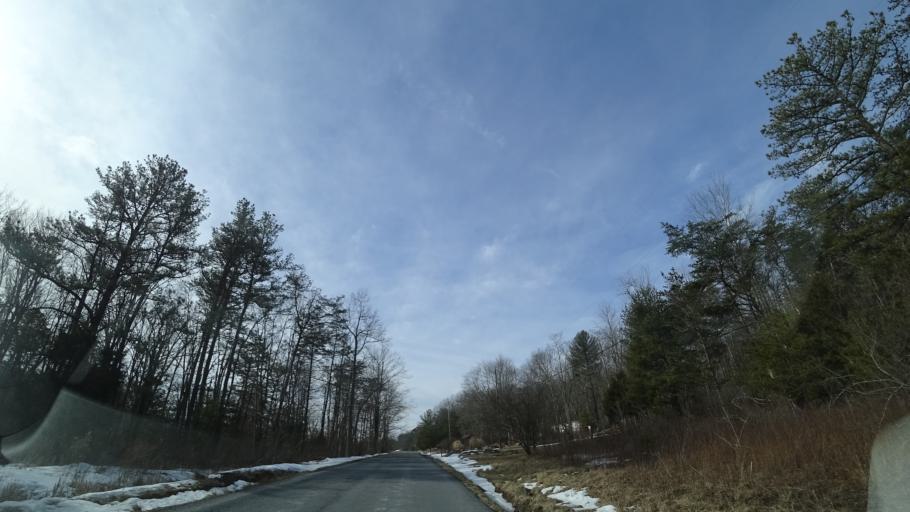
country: US
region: Virginia
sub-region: Shenandoah County
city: Edinburg
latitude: 38.9693
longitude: -78.6754
